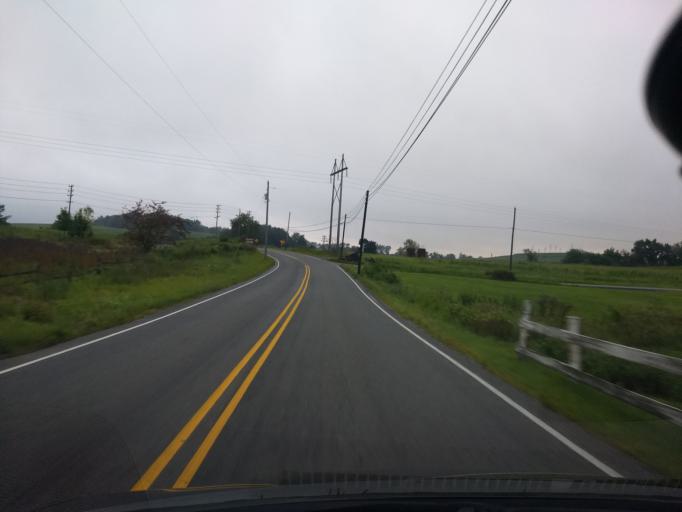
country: US
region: Pennsylvania
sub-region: Westmoreland County
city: Greensburg
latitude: 40.3263
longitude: -79.4885
